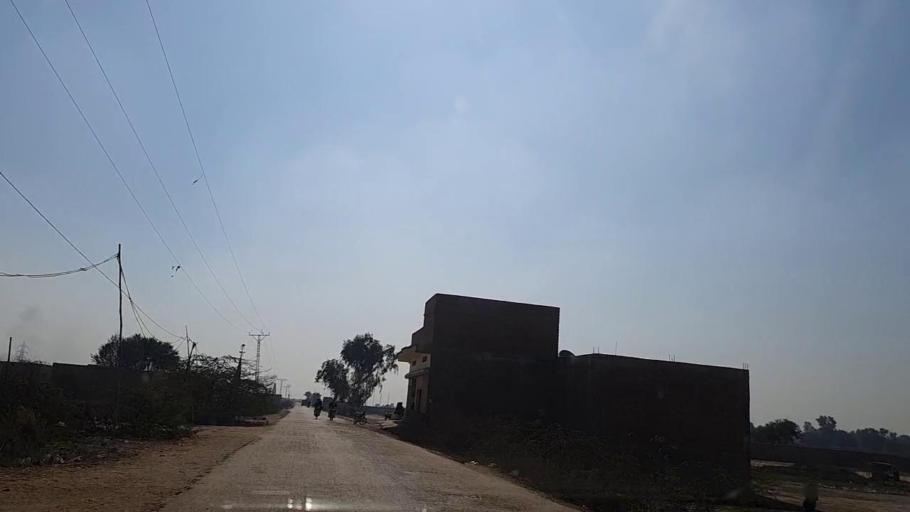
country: PK
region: Sindh
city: Sakrand
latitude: 26.2961
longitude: 68.1080
